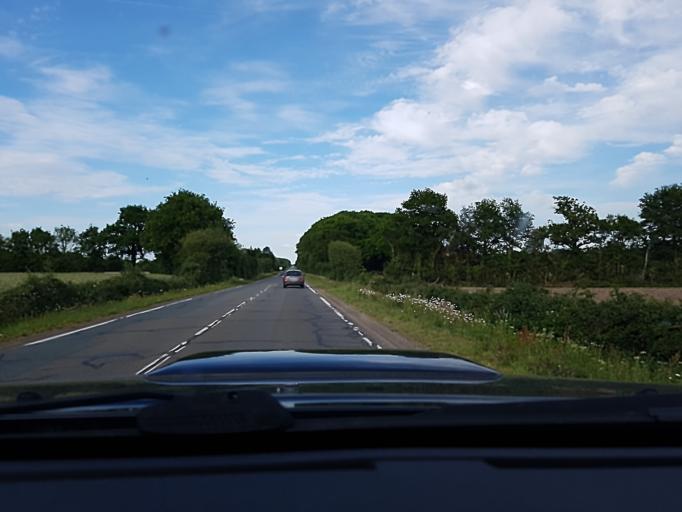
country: FR
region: Pays de la Loire
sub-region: Departement de la Vendee
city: Coex
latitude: 46.7065
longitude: -1.7191
